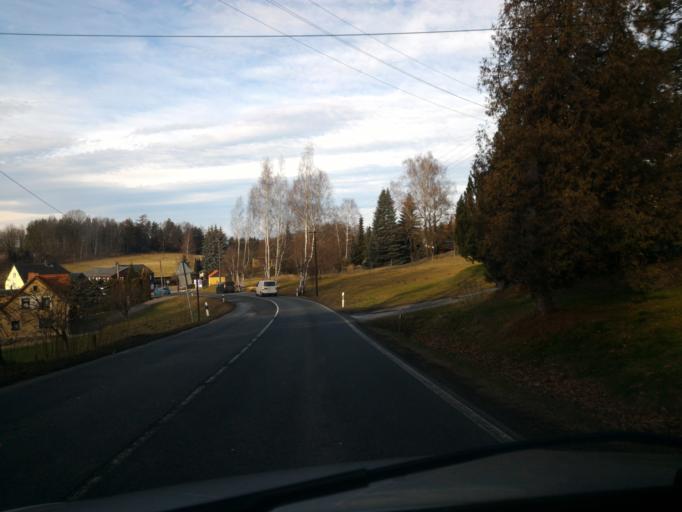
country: DE
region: Saxony
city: Crostau
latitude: 51.0564
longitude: 14.4509
